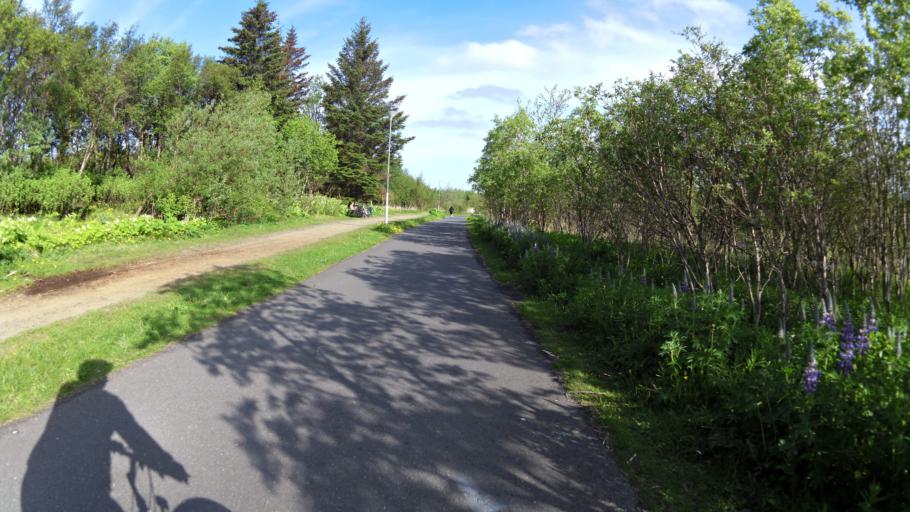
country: IS
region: Capital Region
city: Reykjavik
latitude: 64.1171
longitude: -21.8422
